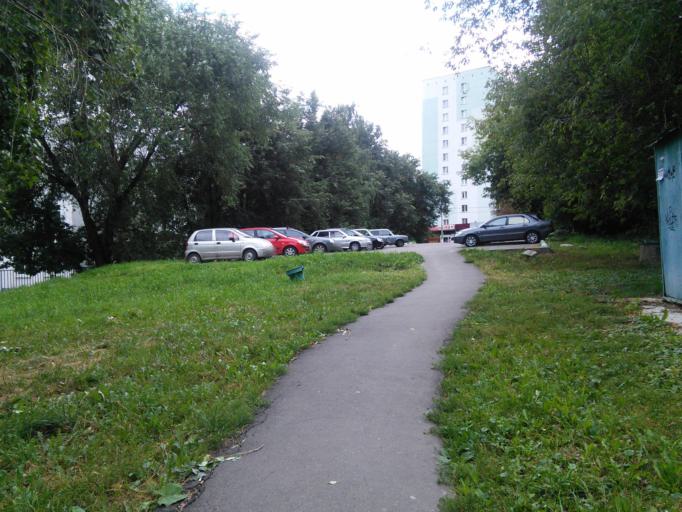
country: RU
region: Moscow
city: Orekhovo-Borisovo Severnoye
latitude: 55.6344
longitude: 37.6773
